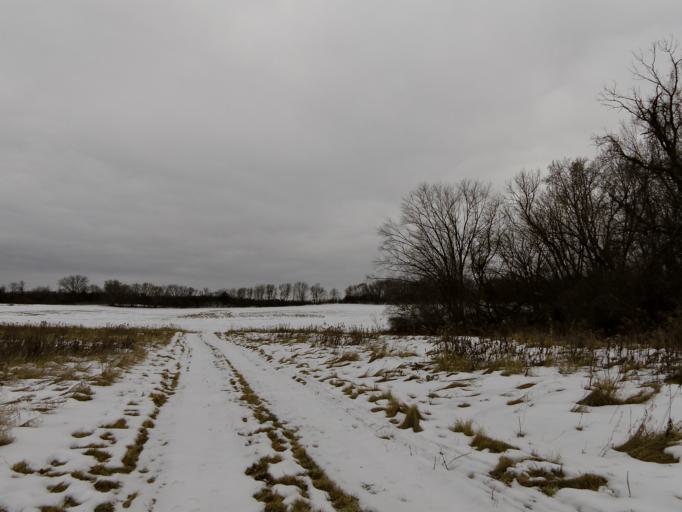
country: US
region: Wisconsin
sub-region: Pierce County
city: Prescott
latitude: 44.7997
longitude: -92.8190
